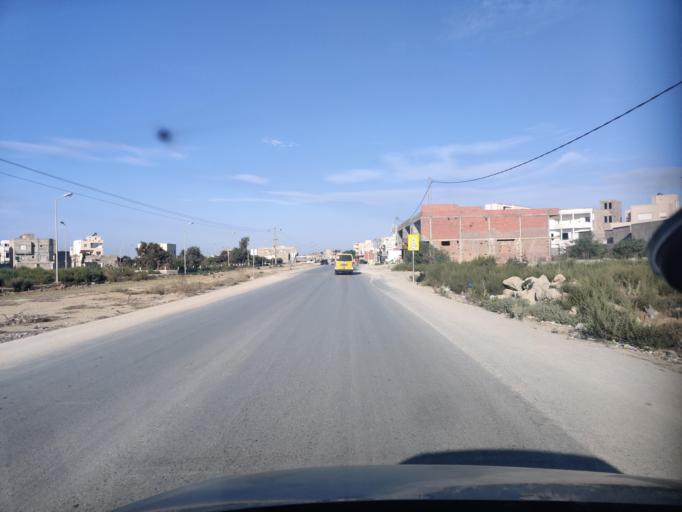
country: TN
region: Ariana
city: Ariana
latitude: 36.9567
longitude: 10.2091
